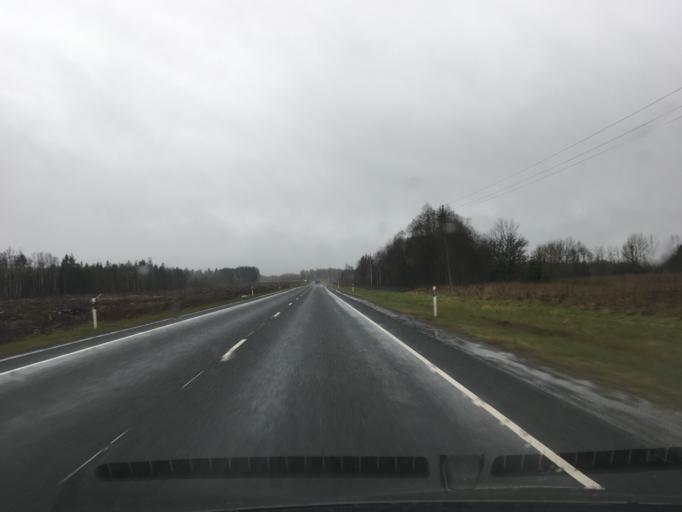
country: EE
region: Harju
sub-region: Nissi vald
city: Turba
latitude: 58.9901
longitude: 24.0582
